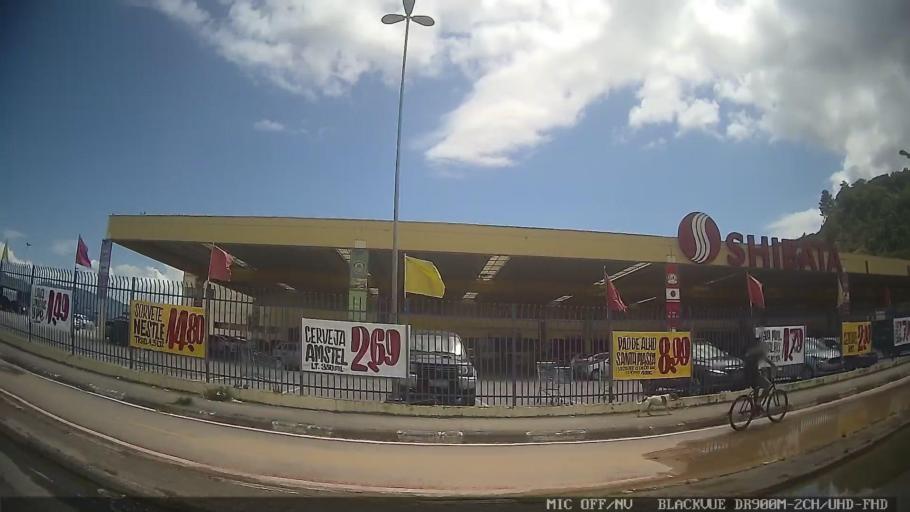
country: BR
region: Sao Paulo
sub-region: Caraguatatuba
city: Caraguatatuba
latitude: -23.6212
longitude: -45.4285
